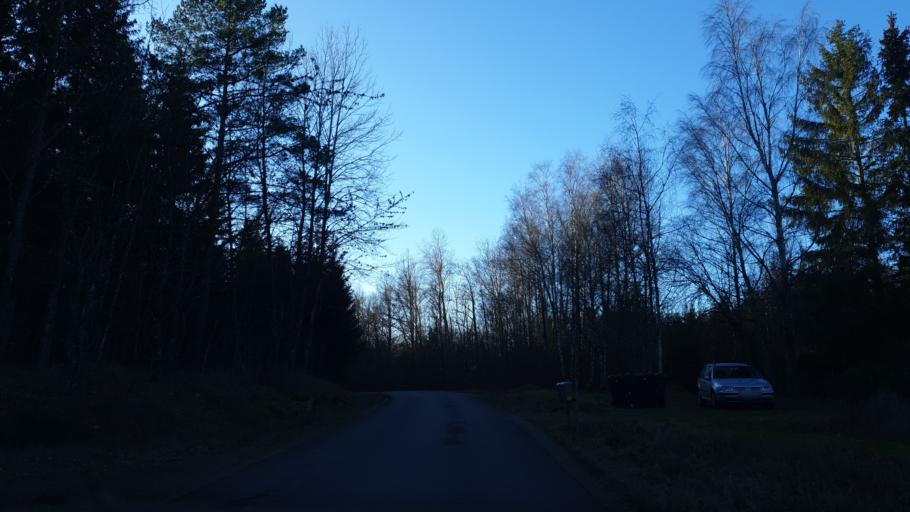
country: SE
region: Blekinge
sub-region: Karlskrona Kommun
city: Nattraby
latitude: 56.2688
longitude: 15.4507
